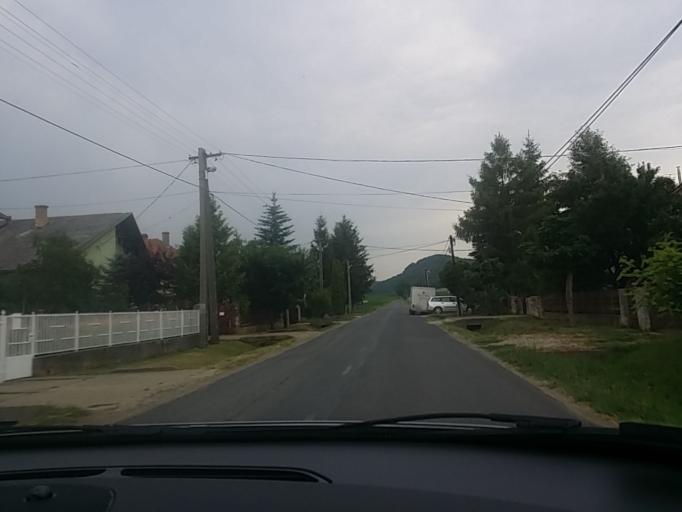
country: HU
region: Borsod-Abauj-Zemplen
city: Arlo
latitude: 48.2238
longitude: 20.1926
